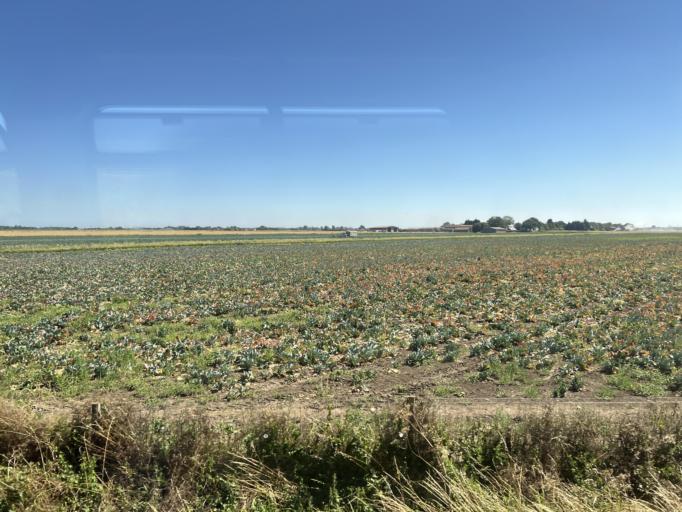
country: GB
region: England
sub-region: Lincolnshire
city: Spilsby
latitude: 53.1000
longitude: 0.1102
